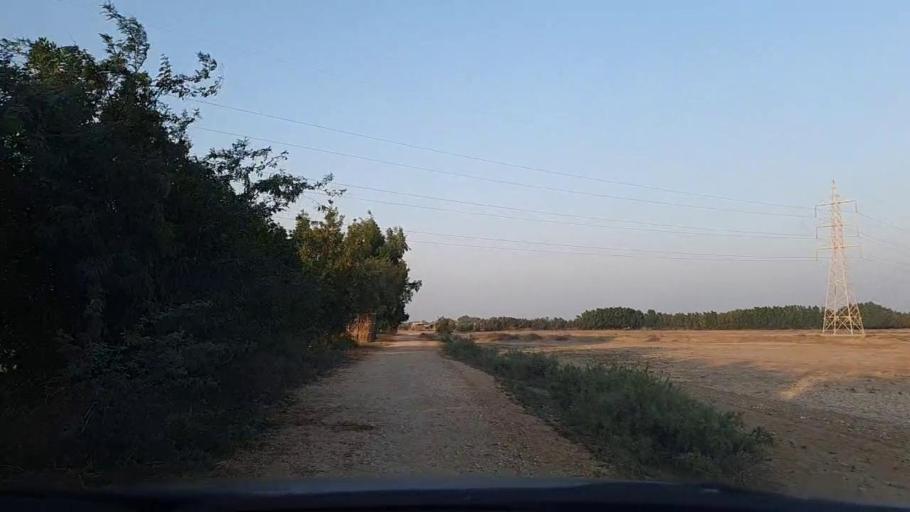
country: PK
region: Sindh
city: Mirpur Sakro
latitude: 24.5619
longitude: 67.6609
